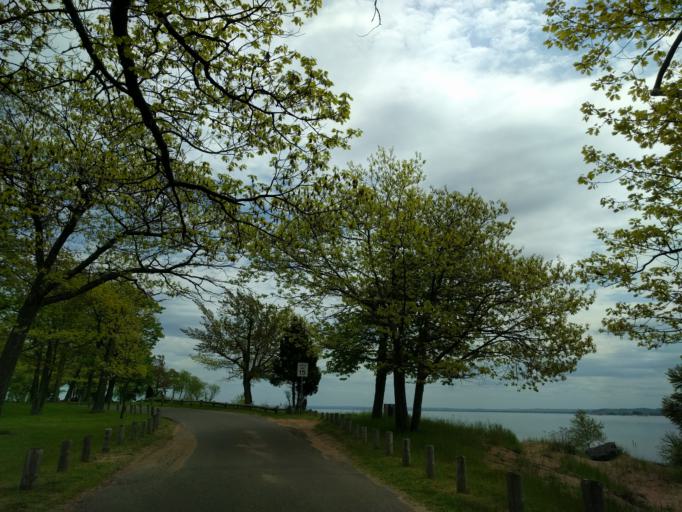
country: US
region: Michigan
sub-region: Marquette County
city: Marquette
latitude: 46.5812
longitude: -87.3835
